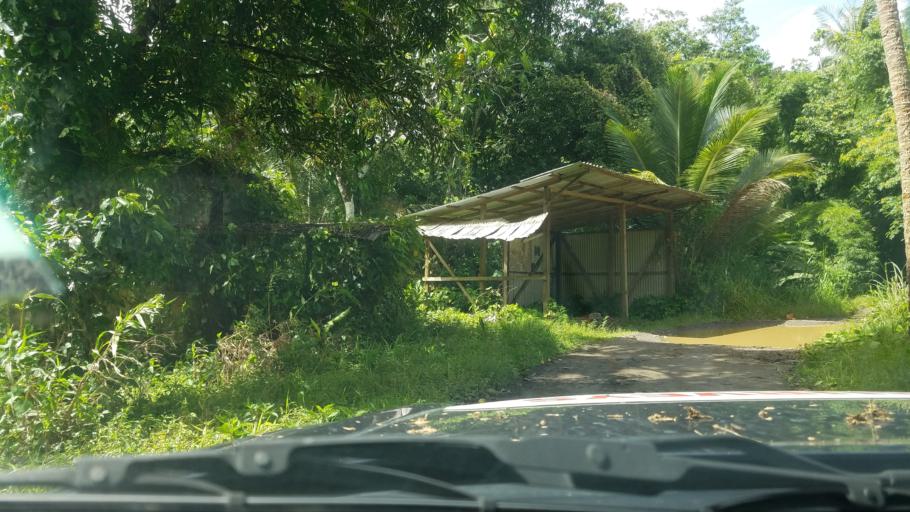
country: LC
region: Anse-la-Raye
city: Anse La Raye
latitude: 13.9418
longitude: -60.9897
